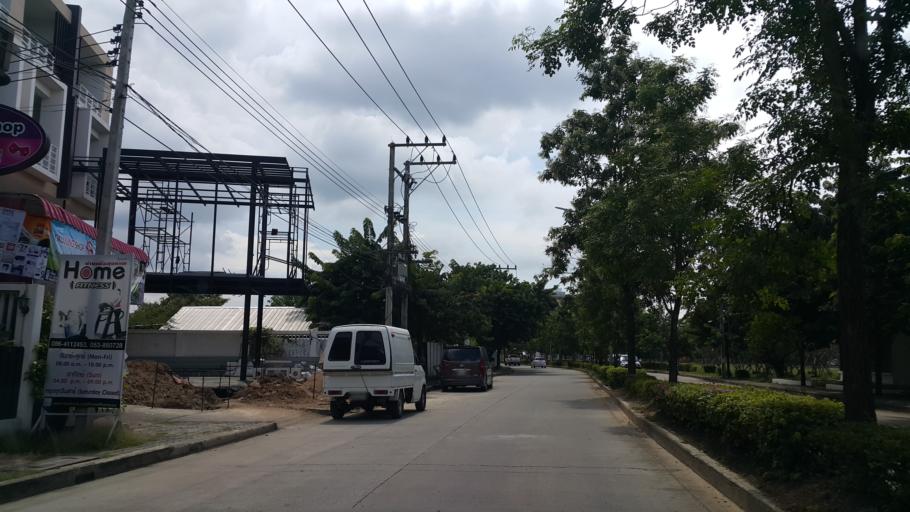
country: TH
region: Chiang Mai
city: Chiang Mai
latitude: 18.8046
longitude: 99.0248
